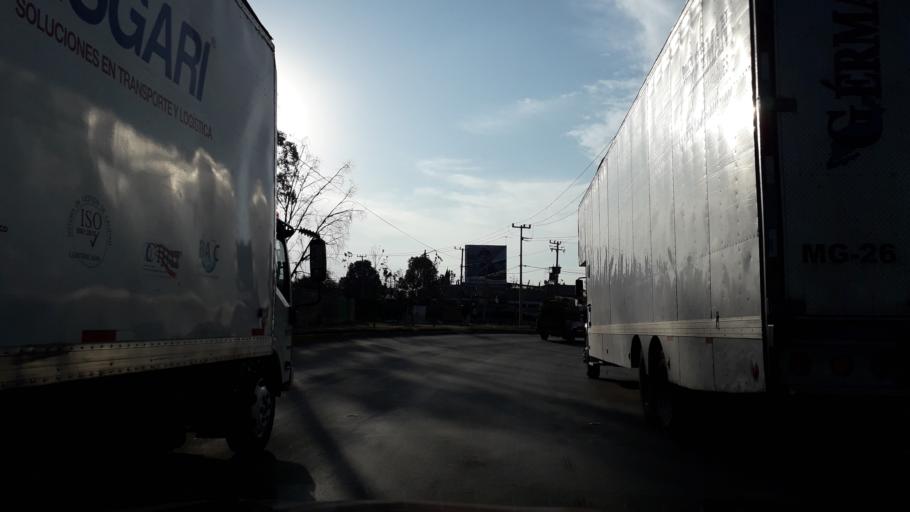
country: MX
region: Mexico City
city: Iztapalapa
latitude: 19.3688
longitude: -99.0462
